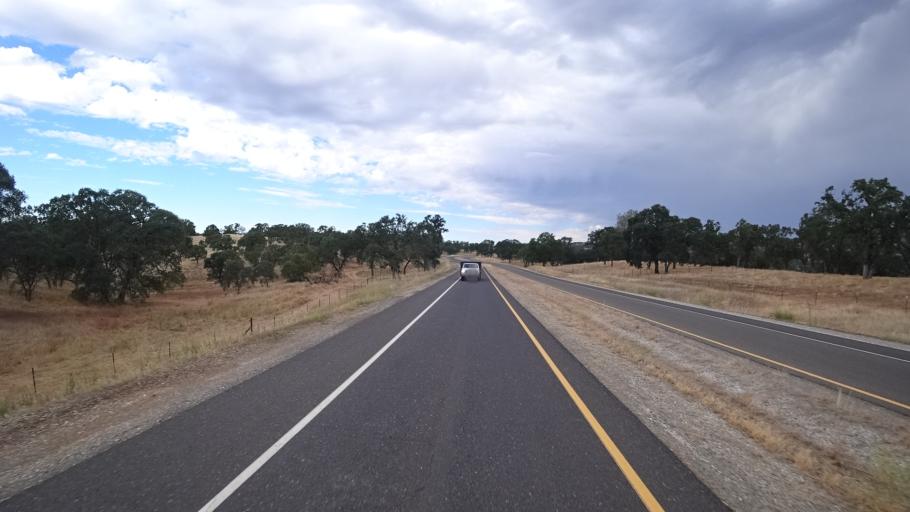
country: US
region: California
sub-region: Calaveras County
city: Copperopolis
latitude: 37.9627
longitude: -120.6540
